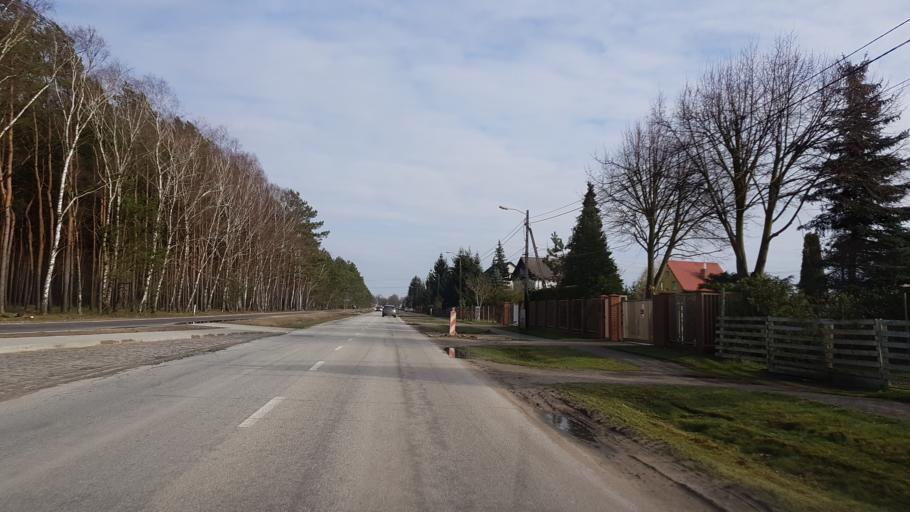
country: PL
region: West Pomeranian Voivodeship
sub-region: Powiat policki
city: Dobra
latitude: 53.4788
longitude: 14.4261
